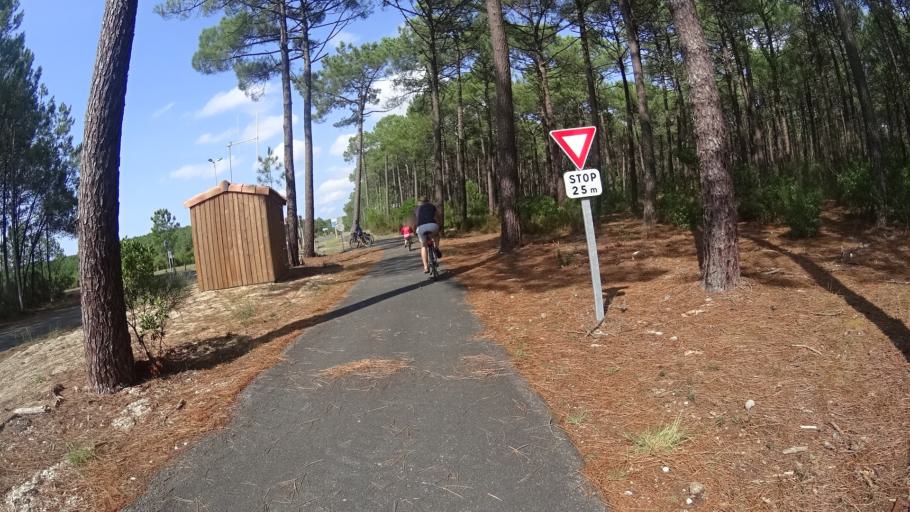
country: FR
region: Aquitaine
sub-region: Departement de la Gironde
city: Lacanau
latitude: 44.9854
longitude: -1.1440
